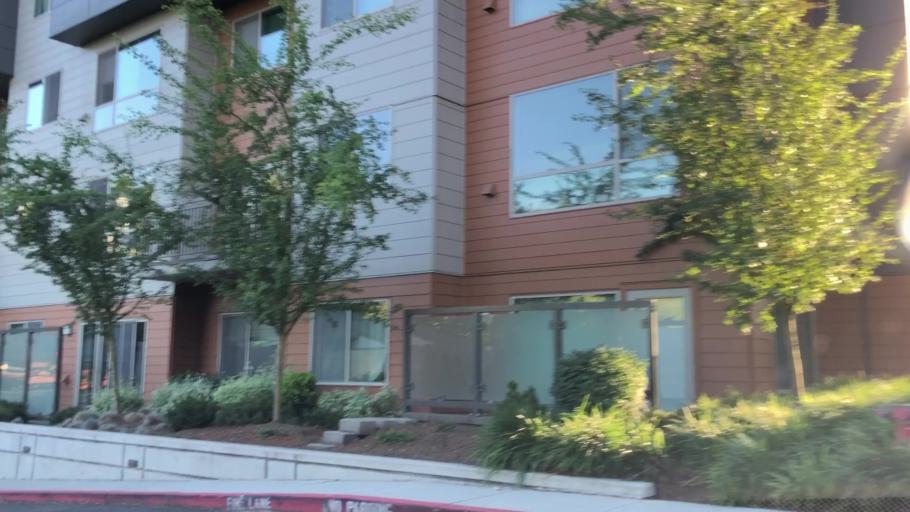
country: US
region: Washington
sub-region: King County
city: Redmond
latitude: 47.6298
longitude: -122.1333
